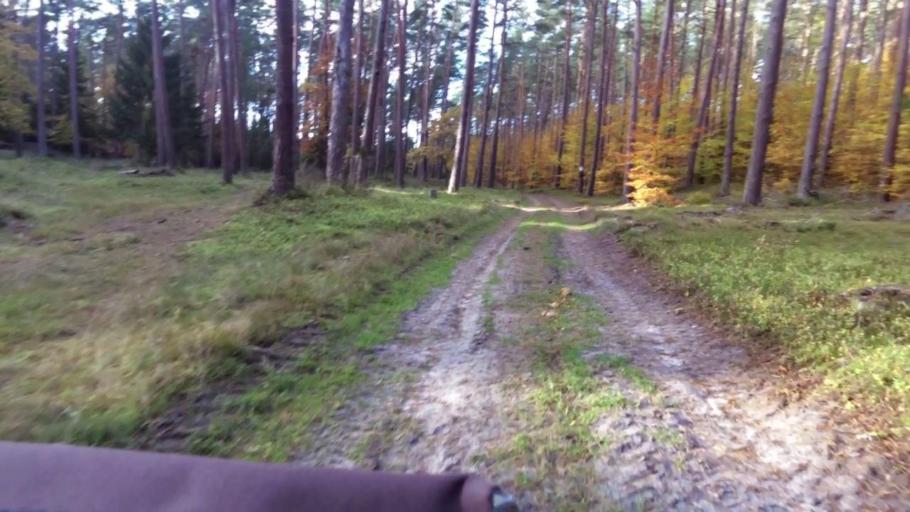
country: PL
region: West Pomeranian Voivodeship
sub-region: Powiat kamienski
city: Miedzyzdroje
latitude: 53.8718
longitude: 14.5196
